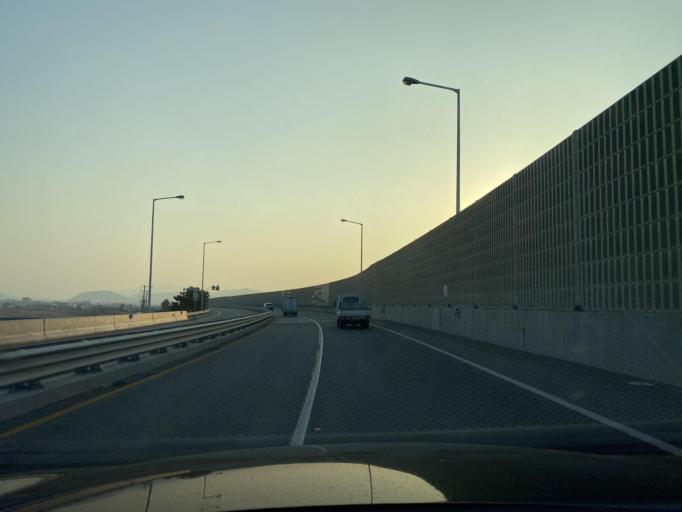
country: KR
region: Chungcheongnam-do
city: Yesan
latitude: 36.7031
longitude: 126.8219
